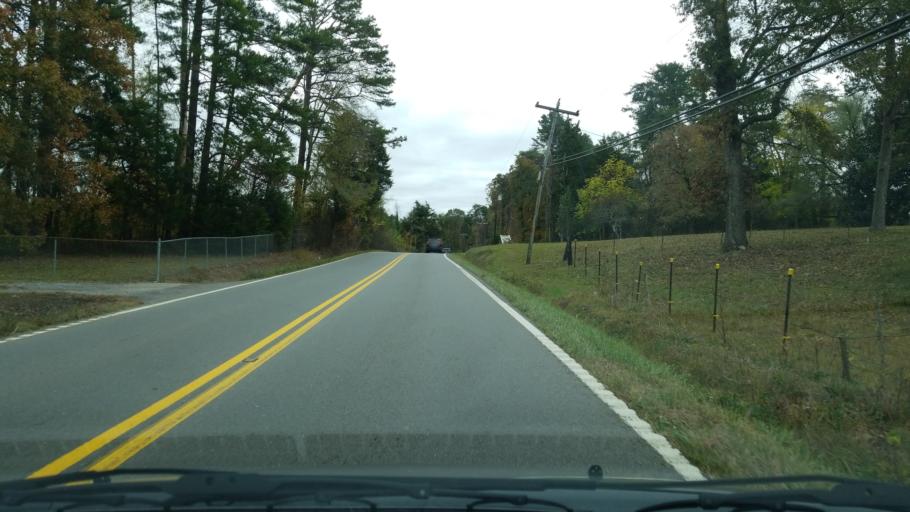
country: US
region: Tennessee
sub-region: Hamilton County
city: Sale Creek
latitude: 35.3700
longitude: -84.9938
